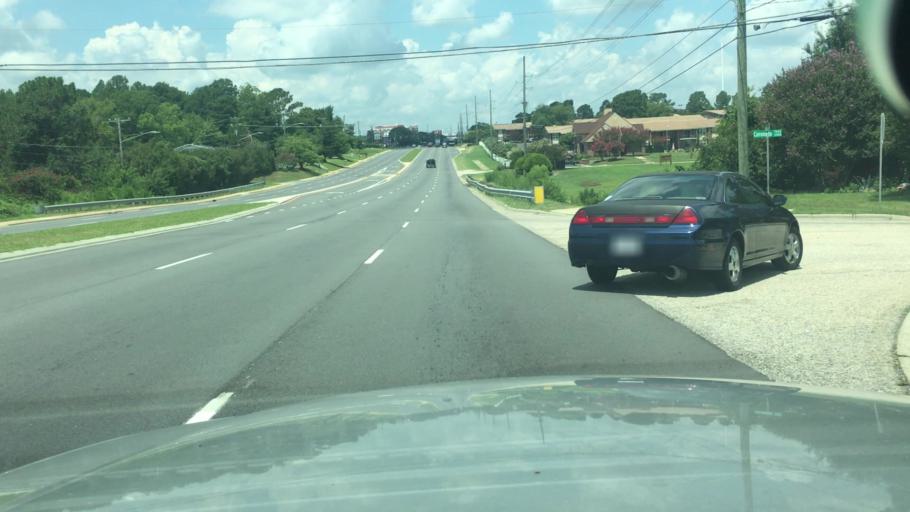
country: US
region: North Carolina
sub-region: Cumberland County
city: Fayetteville
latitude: 35.0244
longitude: -78.9241
